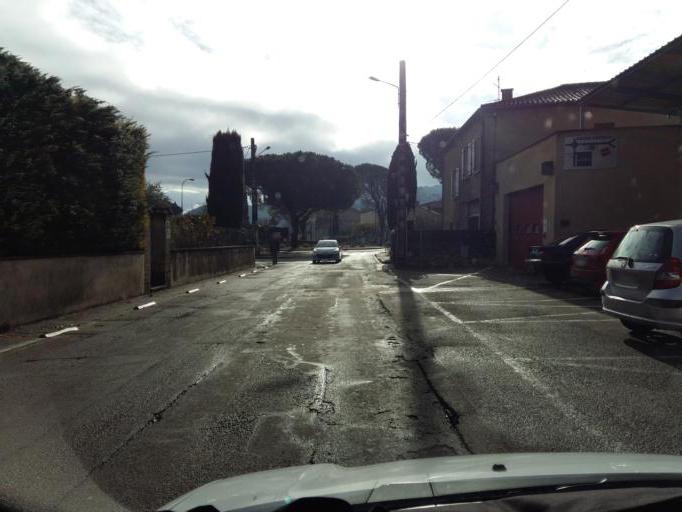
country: FR
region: Provence-Alpes-Cote d'Azur
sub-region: Departement du Vaucluse
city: Vaison-la-Romaine
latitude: 44.2452
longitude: 5.0713
